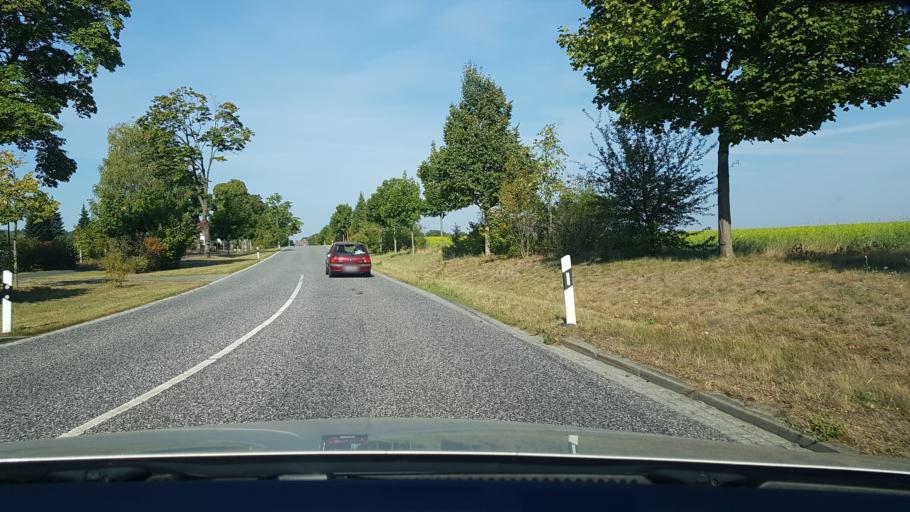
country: DE
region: Brandenburg
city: Mixdorf
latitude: 52.1610
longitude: 14.3856
